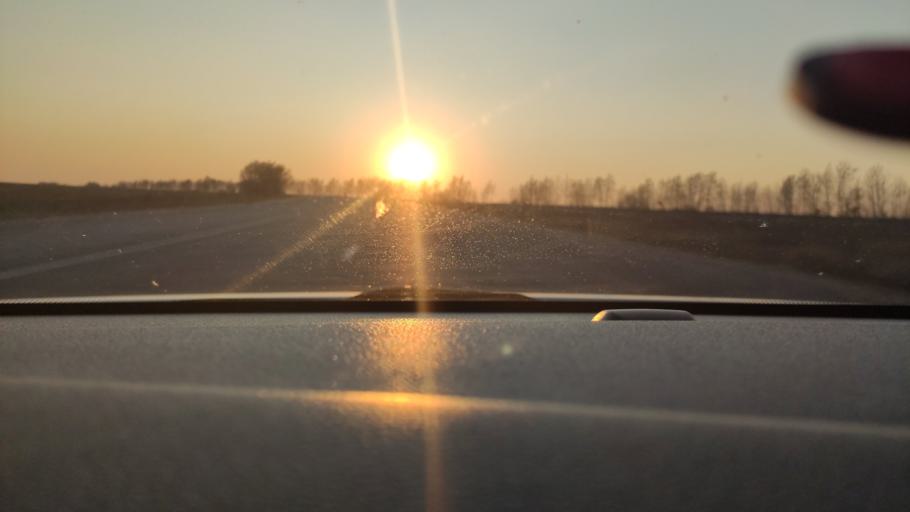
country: RU
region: Voronezj
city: Kolodeznyy
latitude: 51.3283
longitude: 39.1396
